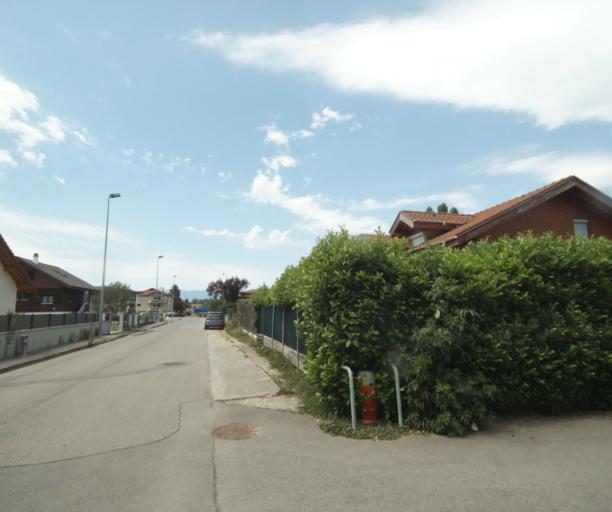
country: FR
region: Rhone-Alpes
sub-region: Departement de la Haute-Savoie
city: Douvaine
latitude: 46.3083
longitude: 6.3128
